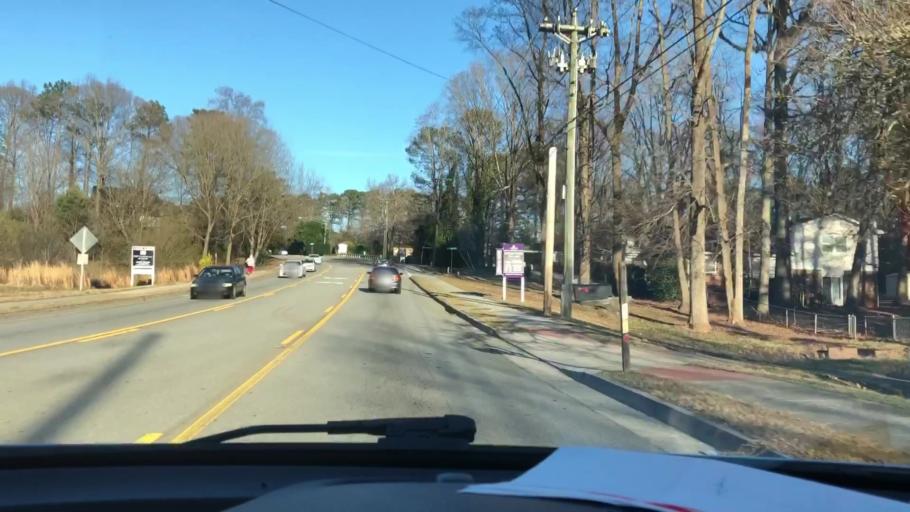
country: US
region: Georgia
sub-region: Gwinnett County
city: Snellville
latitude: 33.8964
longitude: -84.0536
